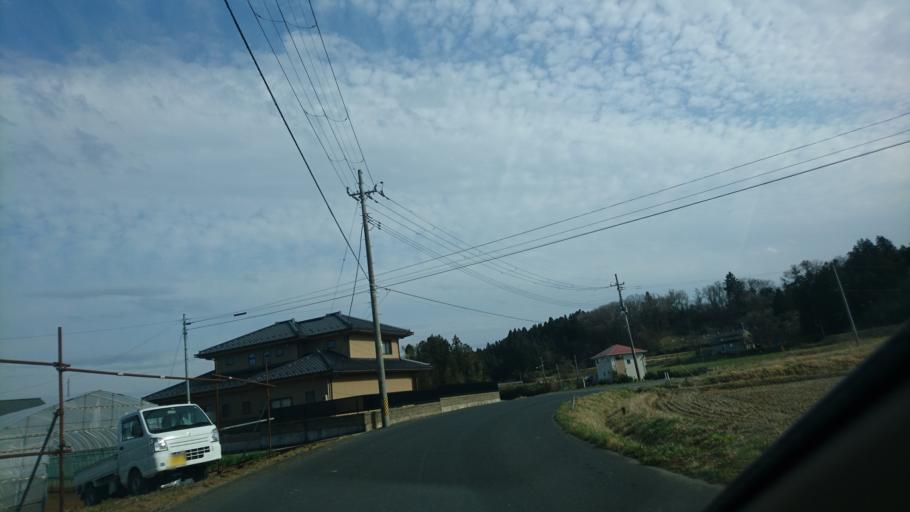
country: JP
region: Iwate
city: Ichinoseki
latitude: 38.8124
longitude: 141.0267
